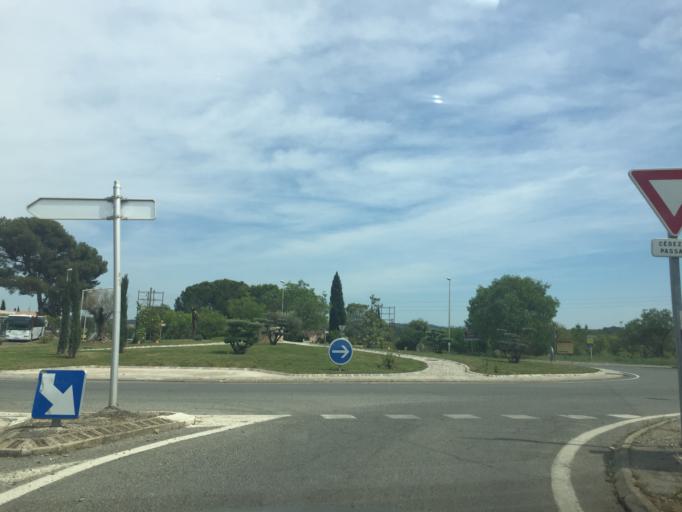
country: FR
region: Provence-Alpes-Cote d'Azur
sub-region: Departement du Var
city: Lorgues
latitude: 43.4922
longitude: 6.3678
